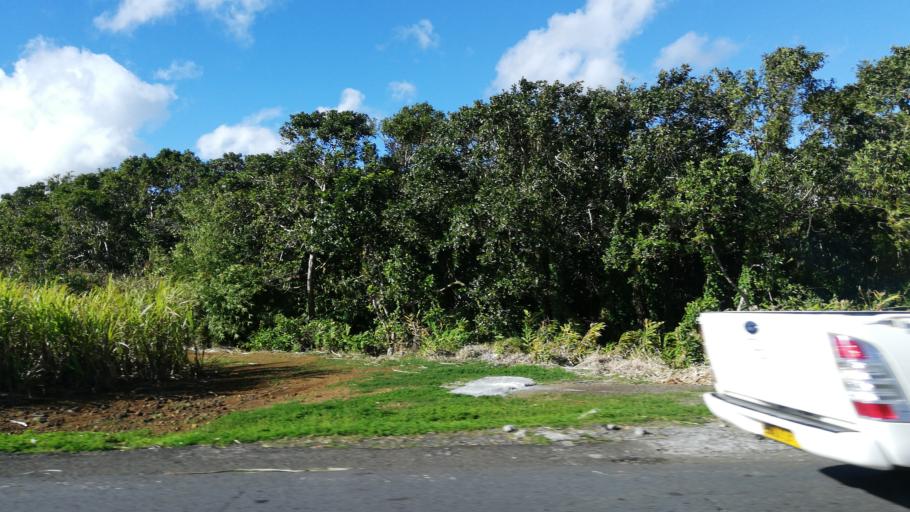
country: MU
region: Moka
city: La Dagotiere
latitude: -20.2322
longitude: 57.5581
